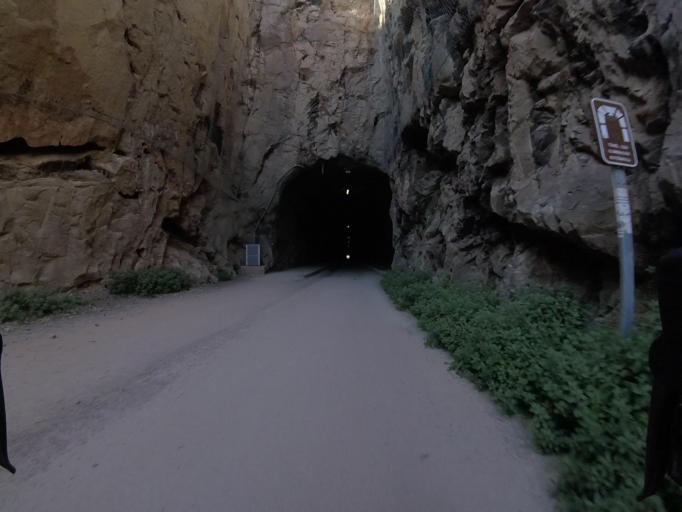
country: ES
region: Valencia
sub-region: Provincia de Castello
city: Orpesa/Oropesa del Mar
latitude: 40.0752
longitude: 0.1314
